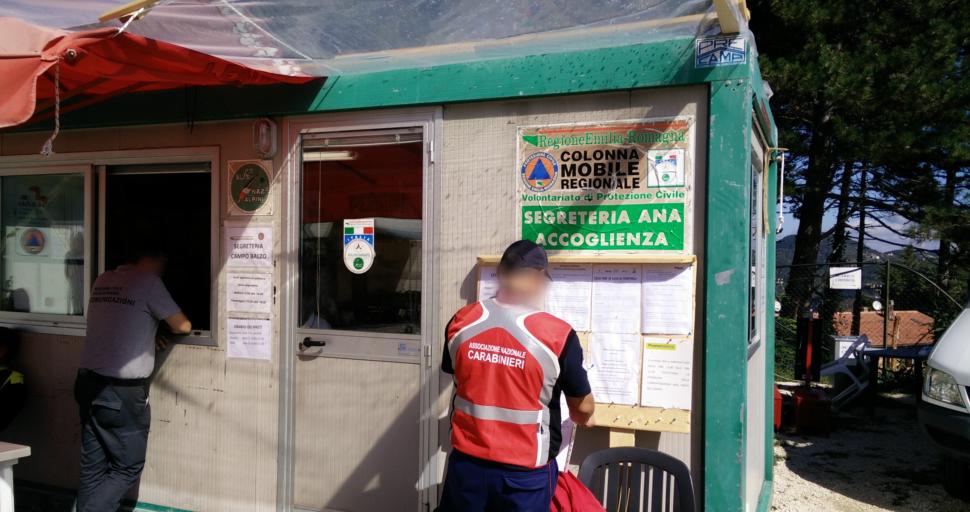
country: IT
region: The Marches
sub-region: Provincia di Ascoli Piceno
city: Balzo
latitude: 42.8391
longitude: 13.3307
